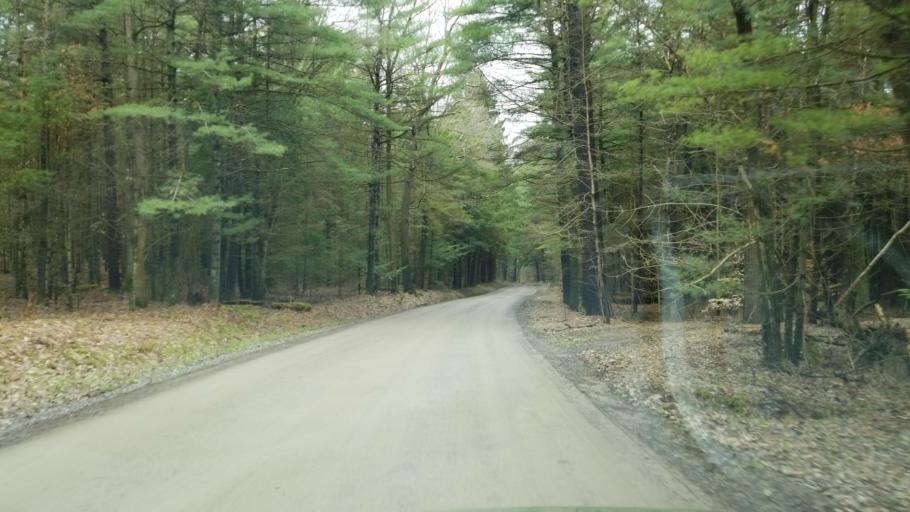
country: US
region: Pennsylvania
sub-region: Clearfield County
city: Shiloh
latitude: 41.1653
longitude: -78.3374
